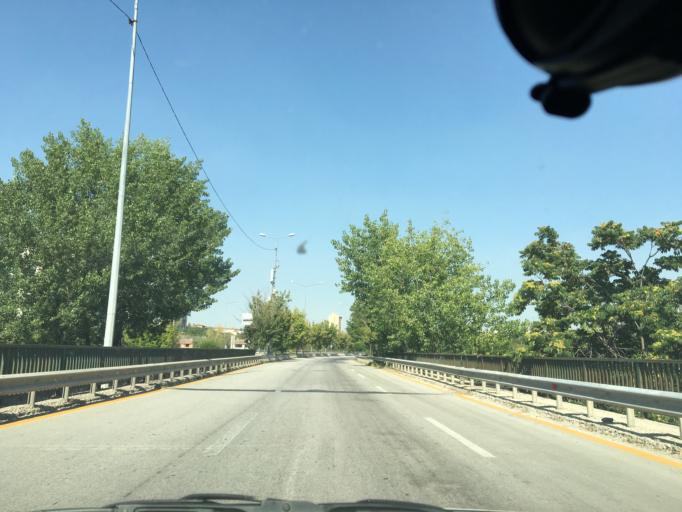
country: TR
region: Ankara
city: Ankara
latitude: 39.9185
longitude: 32.8004
